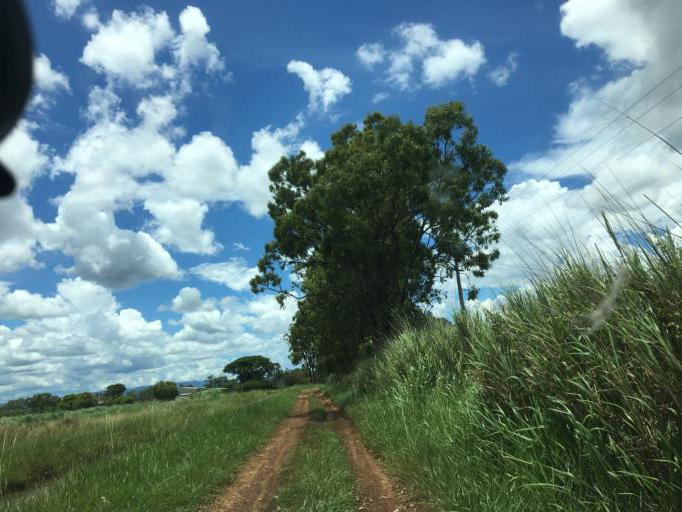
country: AU
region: Queensland
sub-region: Tablelands
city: Mareeba
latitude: -16.9897
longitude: 145.5246
